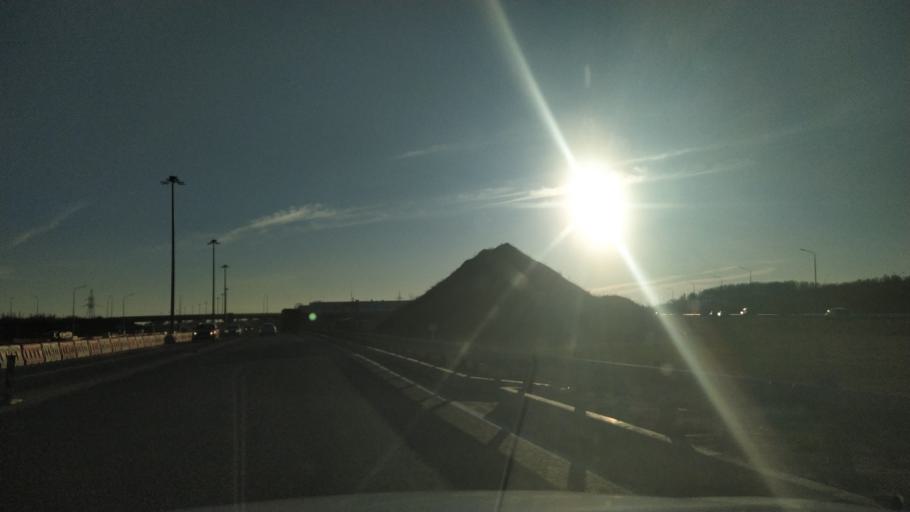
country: RU
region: St.-Petersburg
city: Pargolovo
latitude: 60.0992
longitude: 30.2744
